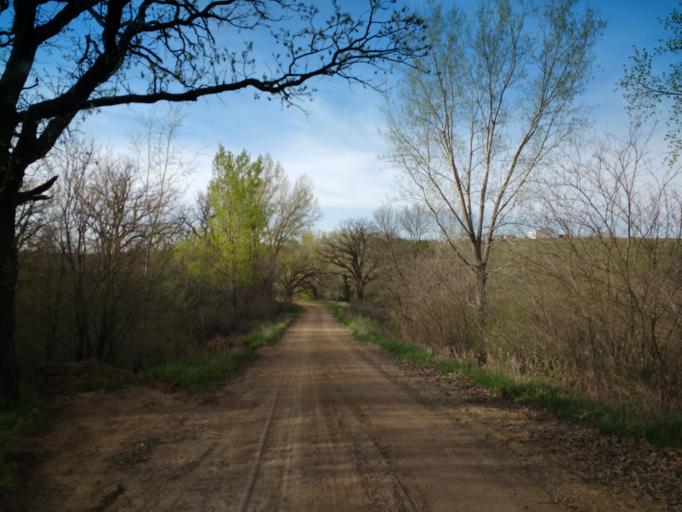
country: US
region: Iowa
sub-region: Plymouth County
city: Kingsley
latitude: 42.5997
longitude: -96.0066
